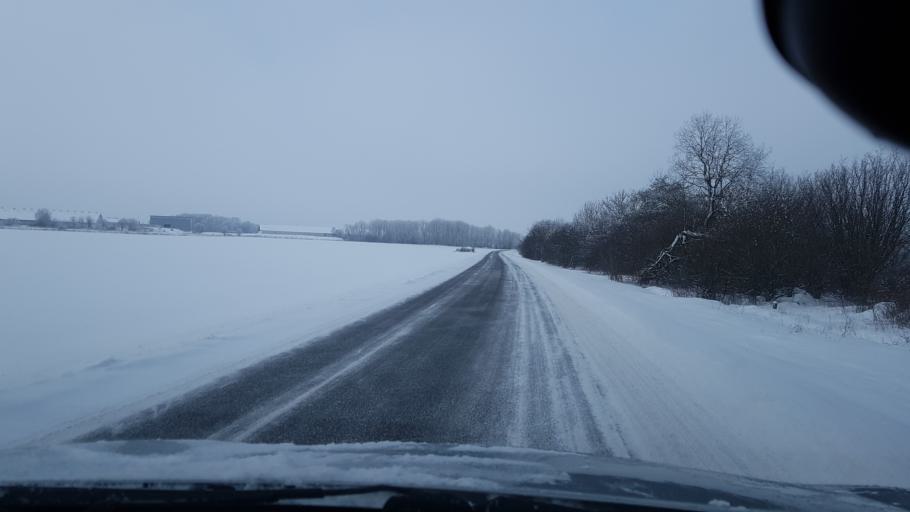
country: EE
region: Harju
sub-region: Keila linn
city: Keila
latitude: 59.3328
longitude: 24.4636
